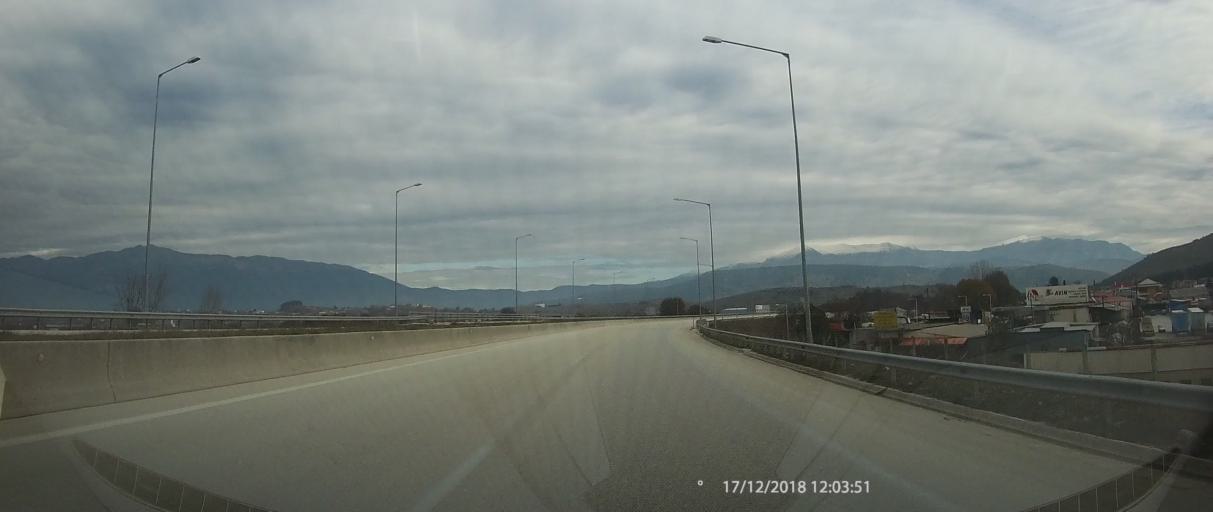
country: GR
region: Epirus
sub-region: Nomos Ioanninon
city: Pedini
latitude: 39.6023
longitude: 20.8685
